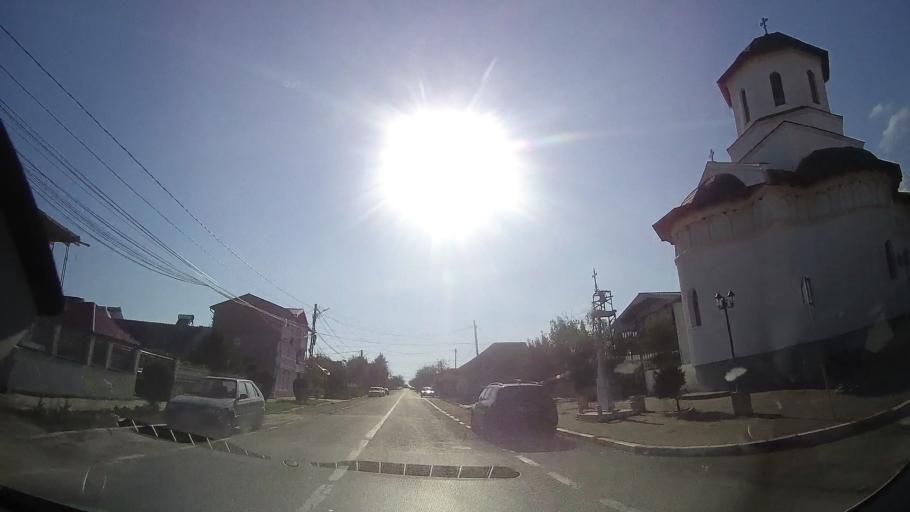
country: RO
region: Constanta
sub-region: Comuna Costinesti
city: Schitu
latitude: 43.9428
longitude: 28.6295
